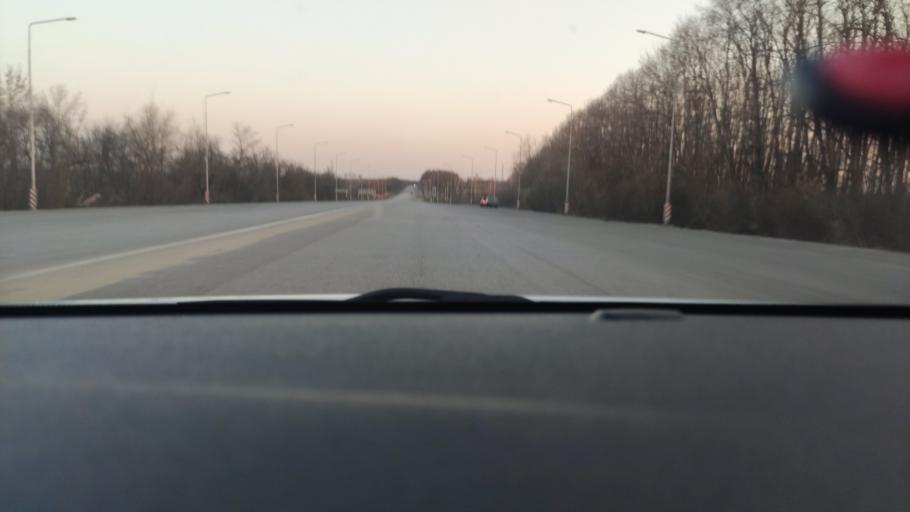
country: RU
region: Voronezj
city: Kolodeznyy
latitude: 51.3351
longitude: 39.0248
